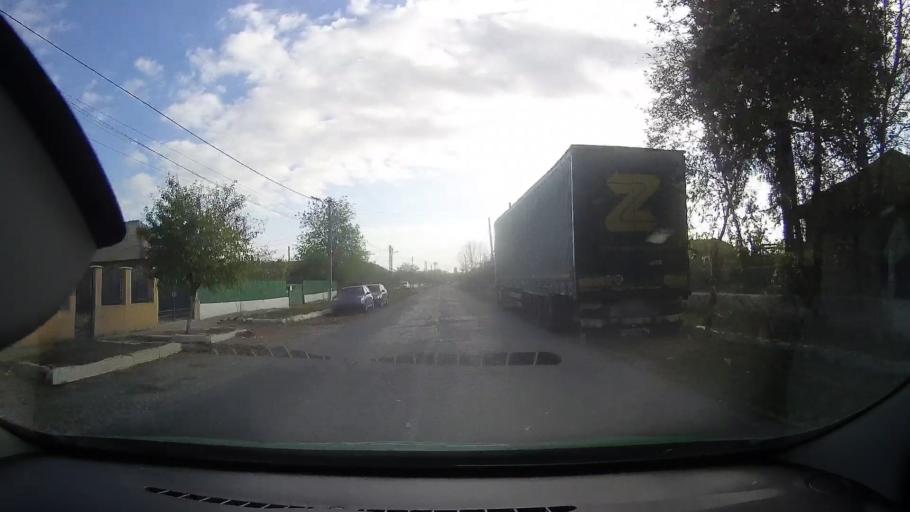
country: RO
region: Constanta
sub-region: Comuna Corbu
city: Corbu
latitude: 44.4222
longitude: 28.6603
